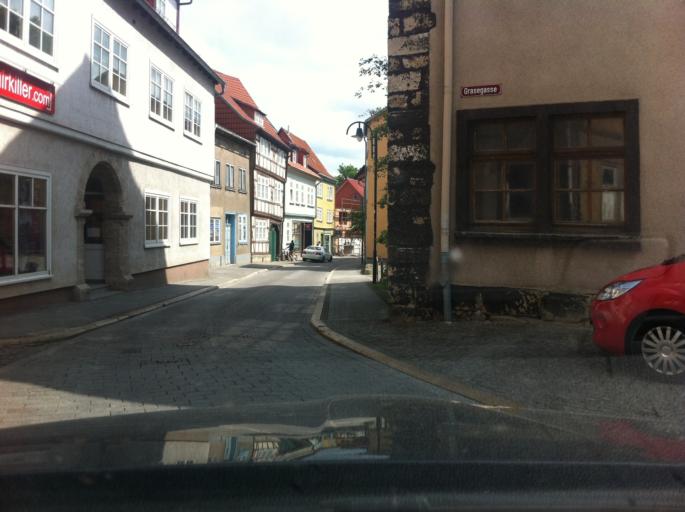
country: DE
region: Thuringia
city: Muehlhausen
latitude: 51.2106
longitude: 10.4576
